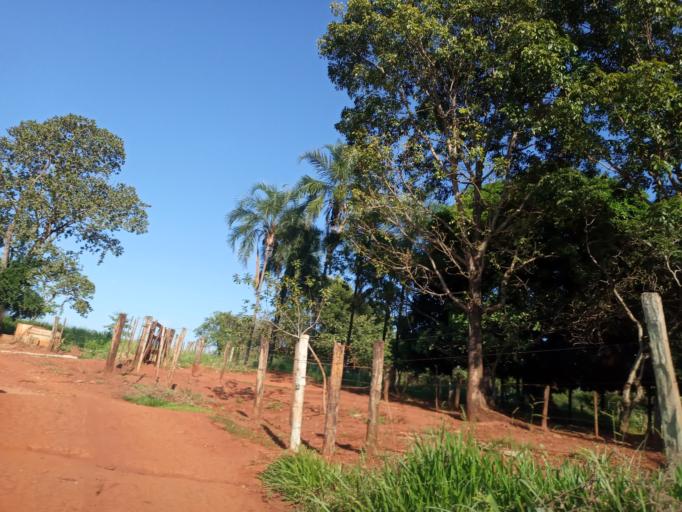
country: BR
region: Minas Gerais
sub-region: Ituiutaba
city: Ituiutaba
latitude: -18.9765
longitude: -49.4970
